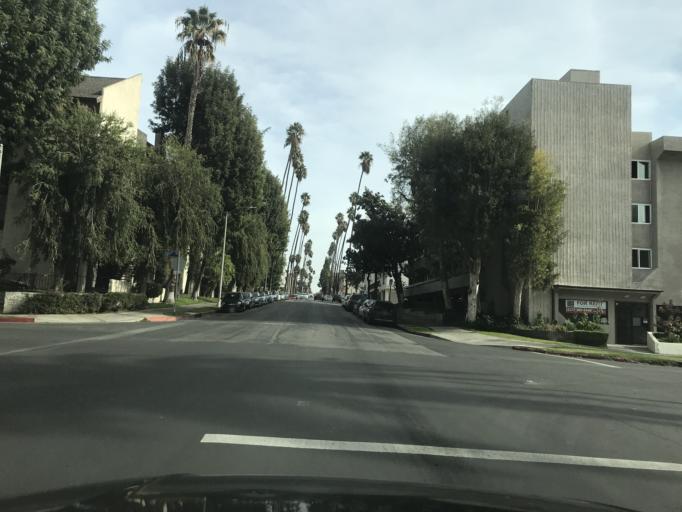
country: US
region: California
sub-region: Los Angeles County
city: Hollywood
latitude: 34.0653
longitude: -118.3056
